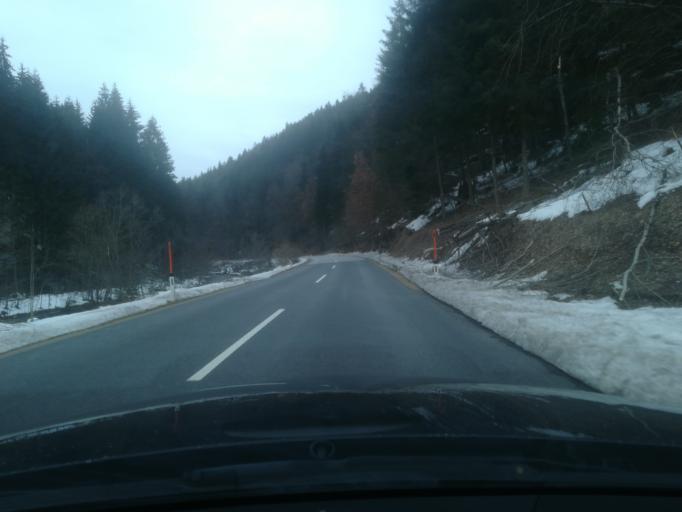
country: AT
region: Upper Austria
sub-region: Politischer Bezirk Perg
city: Perg
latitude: 48.3990
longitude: 14.6377
